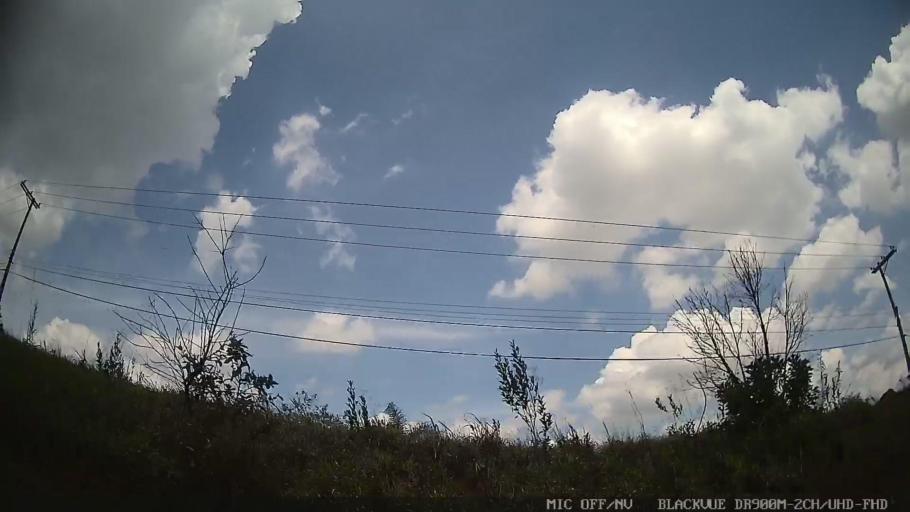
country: BR
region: Sao Paulo
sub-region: Itatiba
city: Itatiba
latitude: -22.9831
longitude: -46.7834
